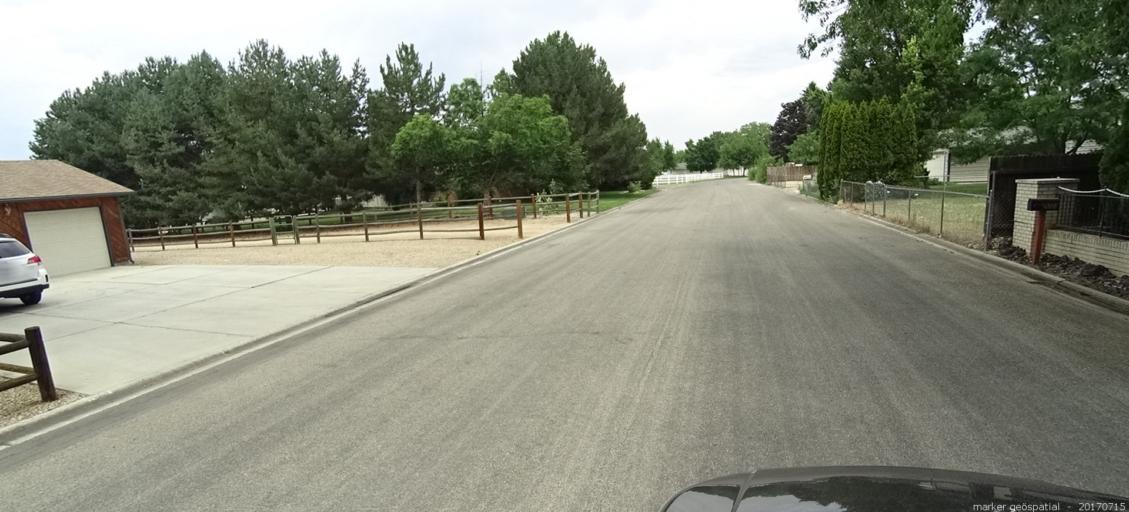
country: US
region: Idaho
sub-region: Ada County
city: Garden City
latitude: 43.5549
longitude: -116.3029
